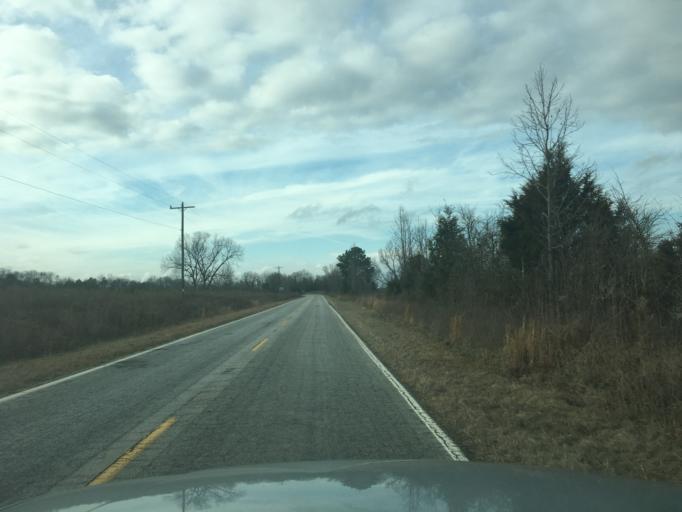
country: US
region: South Carolina
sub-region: Abbeville County
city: Lake Secession
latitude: 34.3551
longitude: -82.5061
